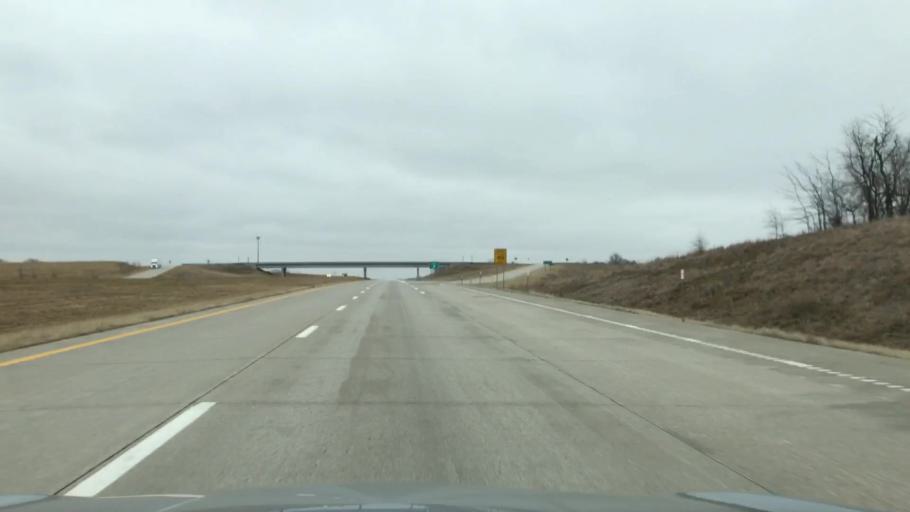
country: US
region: Missouri
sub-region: Linn County
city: Marceline
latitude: 39.7651
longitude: -92.7541
